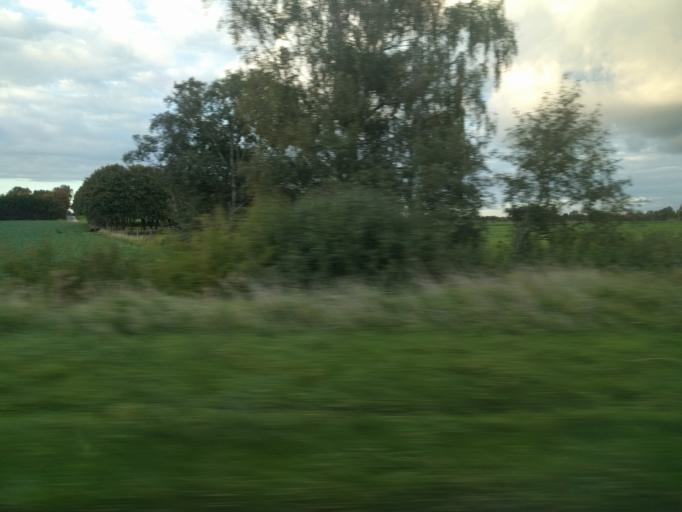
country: DK
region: Zealand
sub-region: Slagelse Kommune
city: Forlev
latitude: 55.3731
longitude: 11.2675
